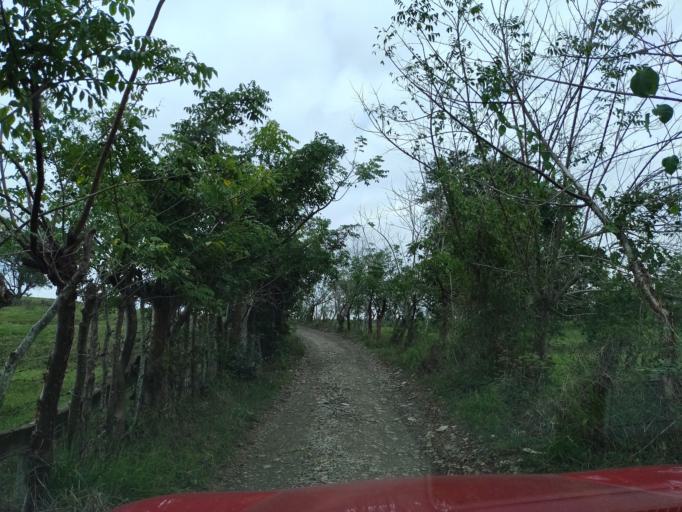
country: MX
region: Veracruz
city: Coatzintla
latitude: 20.4579
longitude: -97.4177
